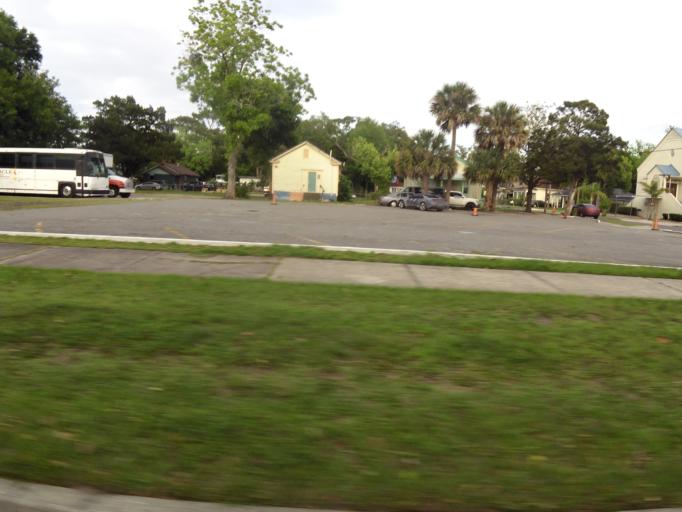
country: US
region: Florida
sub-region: Duval County
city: Jacksonville
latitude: 30.3481
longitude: -81.6431
